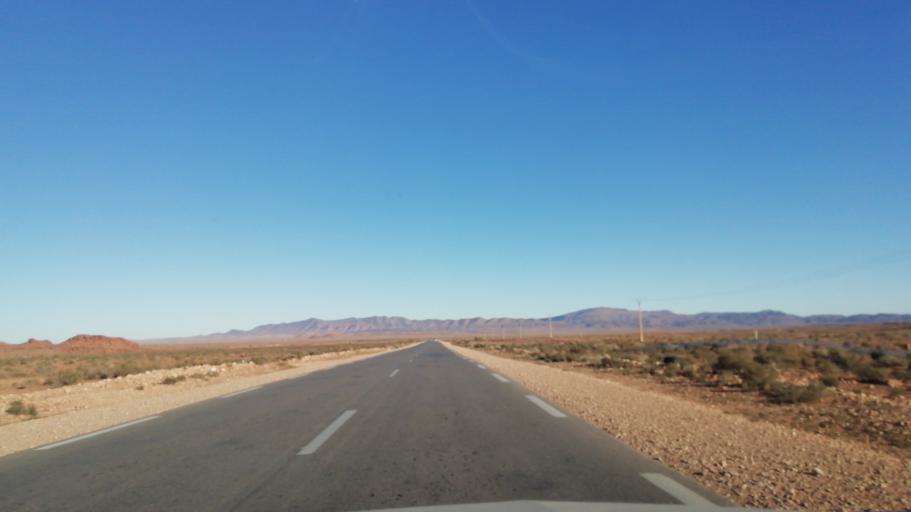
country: DZ
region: El Bayadh
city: El Abiodh Sidi Cheikh
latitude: 33.1700
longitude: 0.5017
